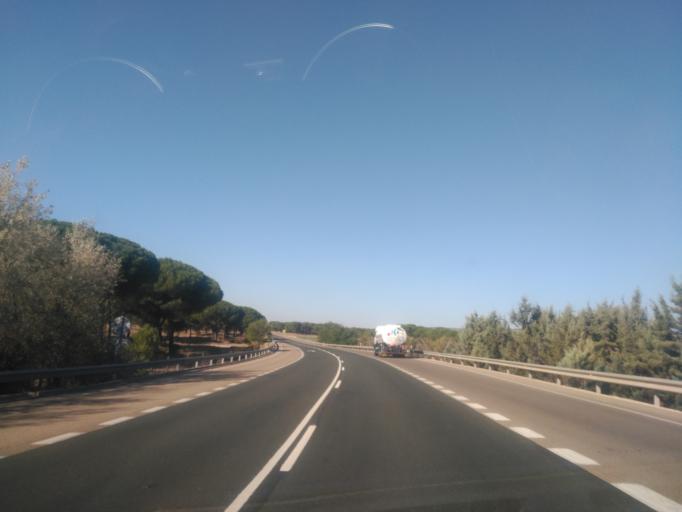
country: ES
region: Castille and Leon
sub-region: Provincia de Valladolid
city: Quintanilla de Onesimo
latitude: 41.6214
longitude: -4.3798
